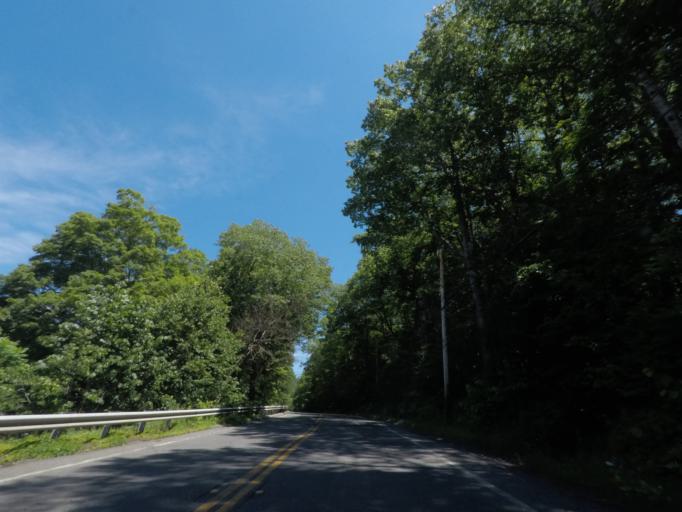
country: US
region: Massachusetts
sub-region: Berkshire County
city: Becket
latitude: 42.2562
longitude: -72.9461
